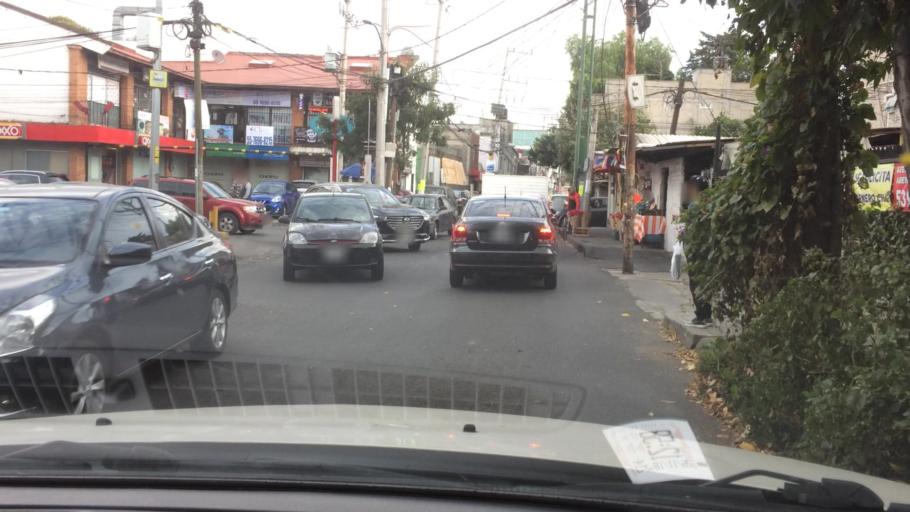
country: MX
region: Mexico City
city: Tlalpan
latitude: 19.2804
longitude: -99.1383
